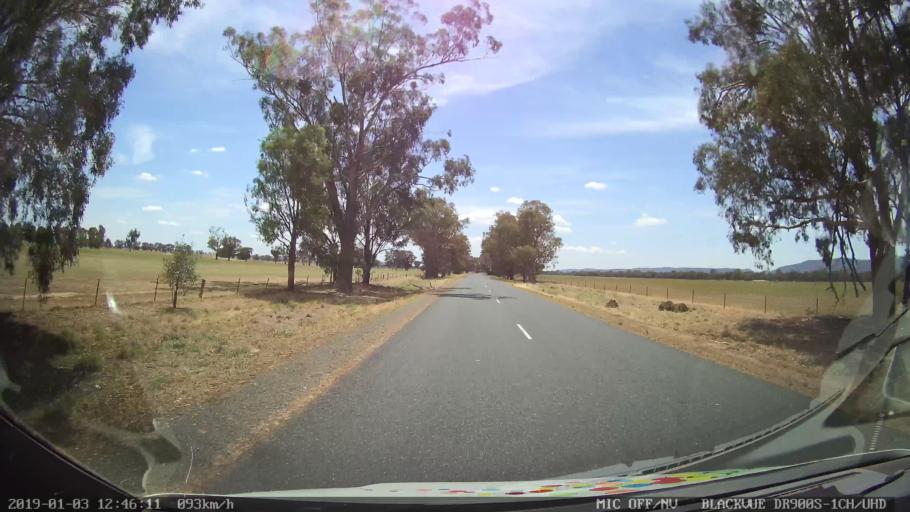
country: AU
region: New South Wales
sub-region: Weddin
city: Grenfell
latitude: -33.7408
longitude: 148.2305
